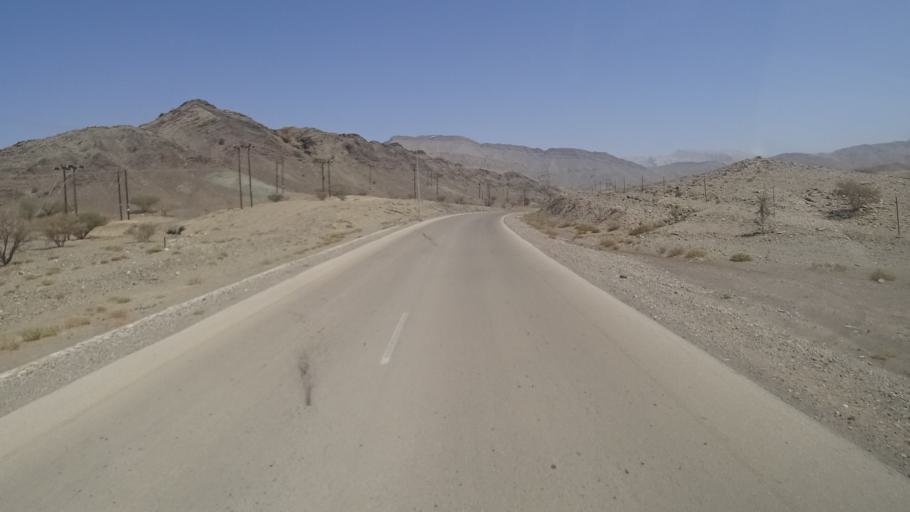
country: OM
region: Ash Sharqiyah
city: Badiyah
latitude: 22.5574
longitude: 59.0169
